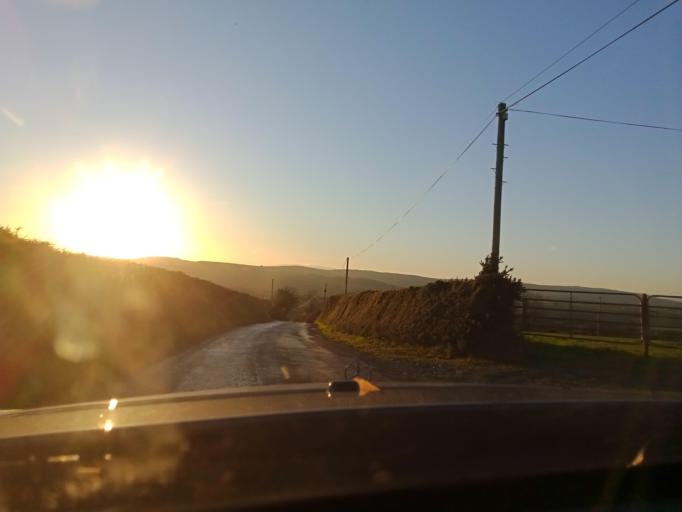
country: IE
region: Munster
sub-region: Waterford
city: Waterford
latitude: 52.3700
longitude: -7.1482
